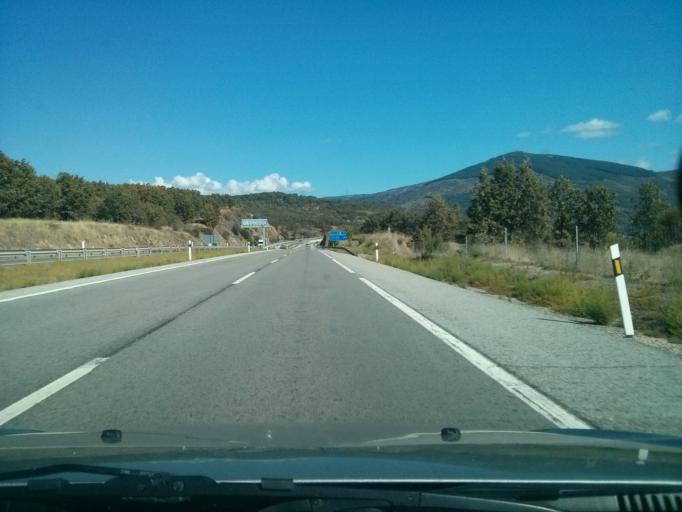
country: ES
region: Madrid
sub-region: Provincia de Madrid
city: Horcajo de la Sierra
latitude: 41.0713
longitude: -3.6056
